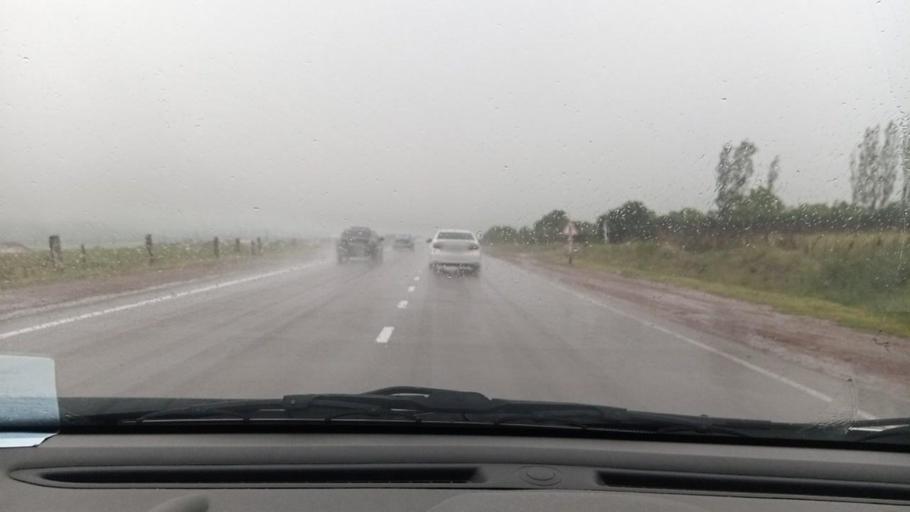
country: UZ
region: Toshkent
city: Angren
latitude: 41.0487
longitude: 70.1568
